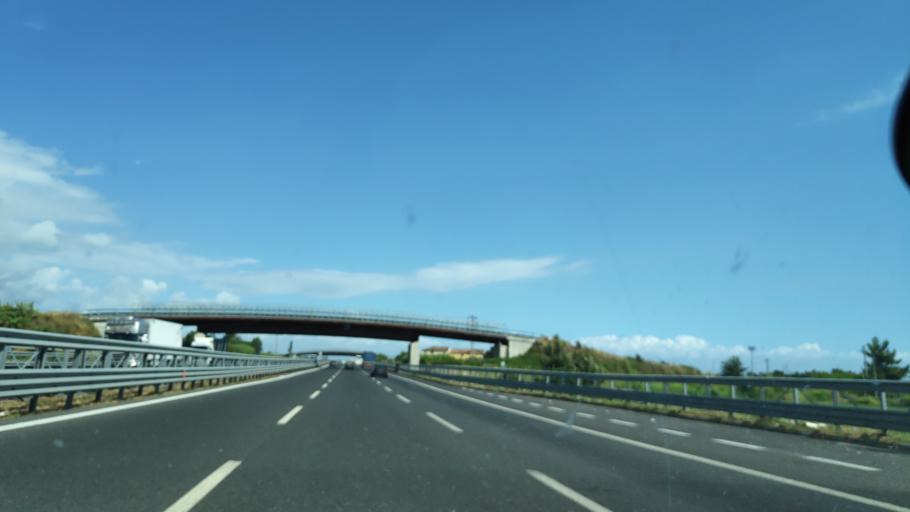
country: IT
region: Campania
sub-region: Provincia di Salerno
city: Pontecagnano
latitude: 40.6505
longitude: 14.8780
